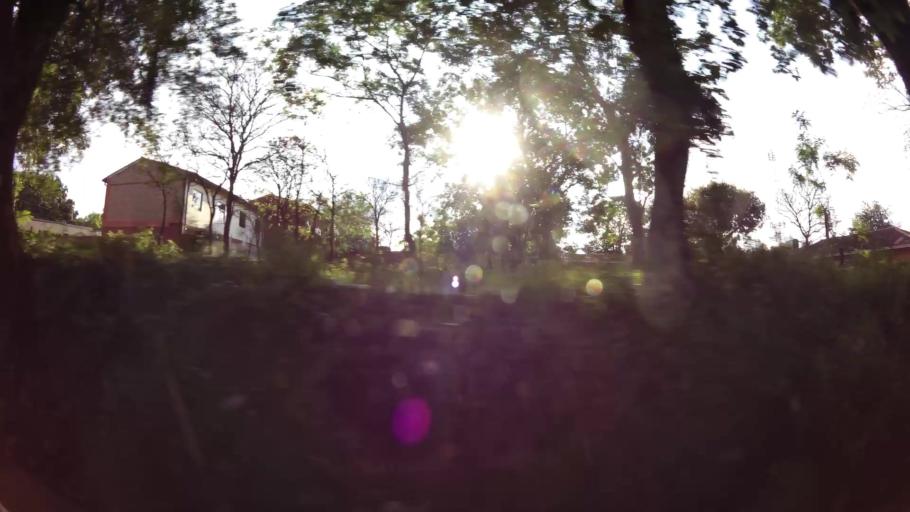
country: PY
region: Central
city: Fernando de la Mora
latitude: -25.3479
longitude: -57.5200
